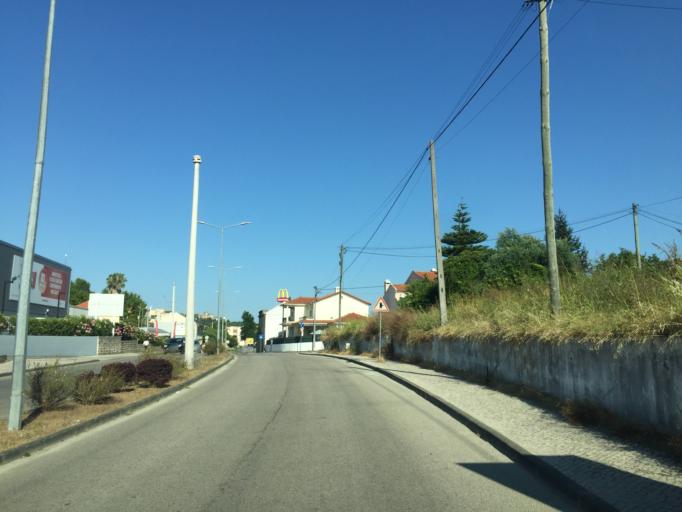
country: PT
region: Santarem
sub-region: Tomar
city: Tomar
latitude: 39.6026
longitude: -8.3971
